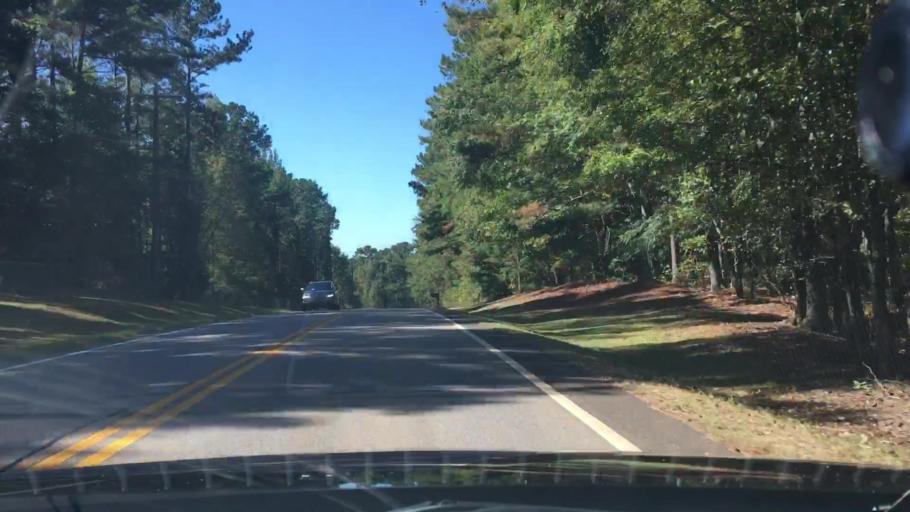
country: US
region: Georgia
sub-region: Fulton County
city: Palmetto
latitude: 33.4478
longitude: -84.6650
